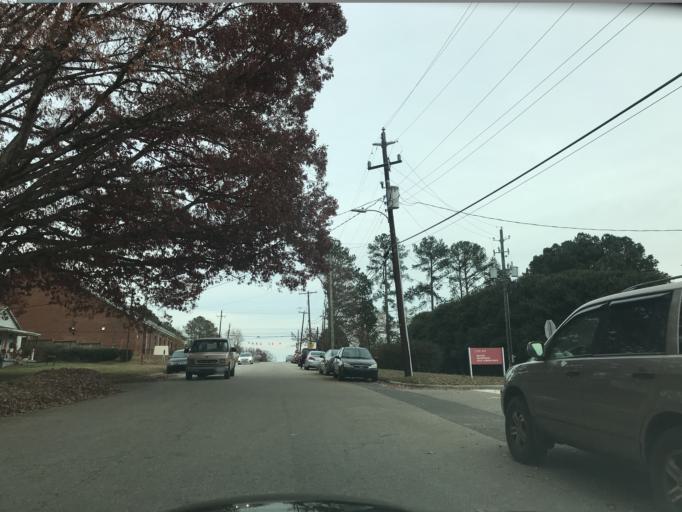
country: US
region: North Carolina
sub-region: Wake County
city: West Raleigh
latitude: 35.7893
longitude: -78.6954
